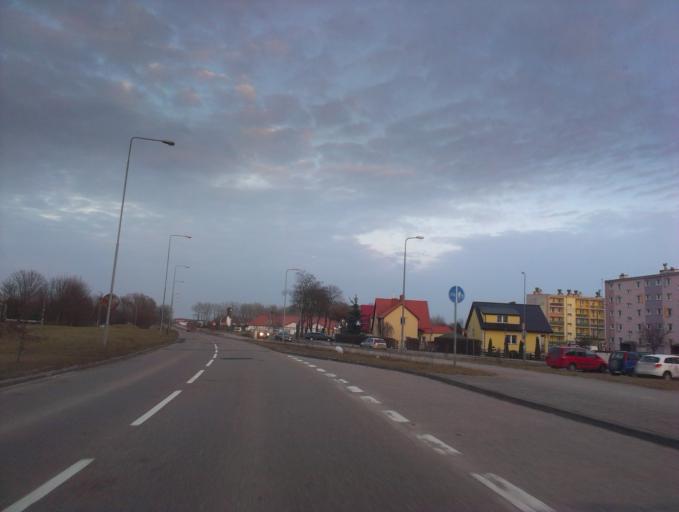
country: PL
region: West Pomeranian Voivodeship
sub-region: Powiat szczecinecki
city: Szczecinek
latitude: 53.7216
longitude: 16.6662
